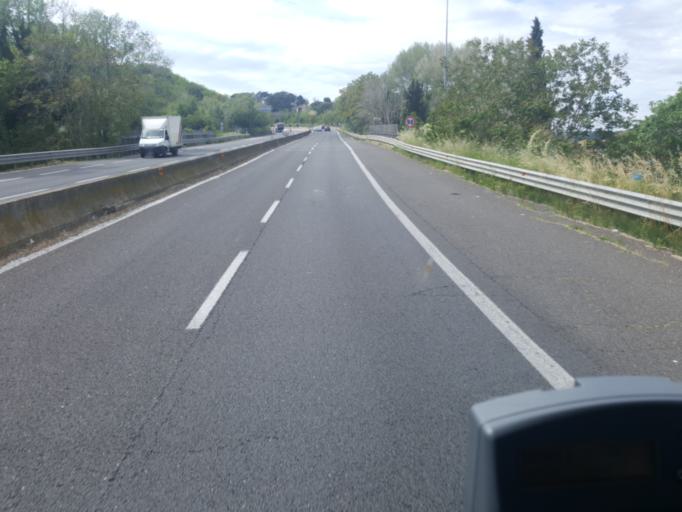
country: IT
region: Latium
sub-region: Citta metropolitana di Roma Capitale
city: Ara Nova
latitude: 41.9077
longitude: 12.2630
